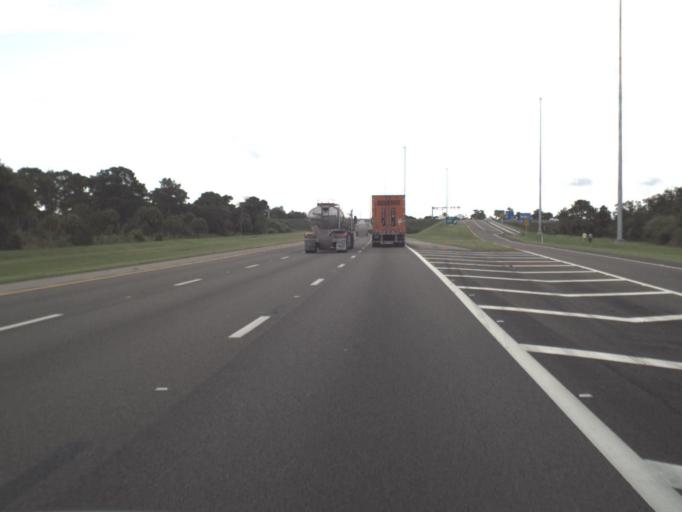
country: US
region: Florida
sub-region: Sarasota County
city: Nokomis
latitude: 27.1418
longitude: -82.4138
